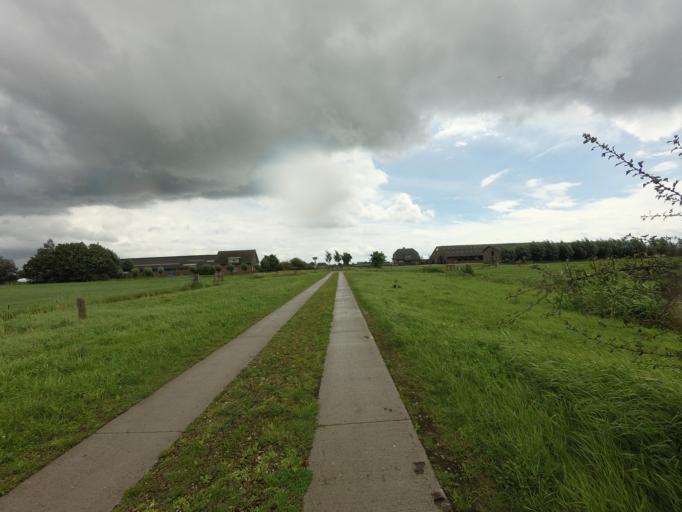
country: NL
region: North Holland
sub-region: Gemeente Wijdemeren
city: Nieuw-Loosdrecht
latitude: 52.1672
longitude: 5.1454
